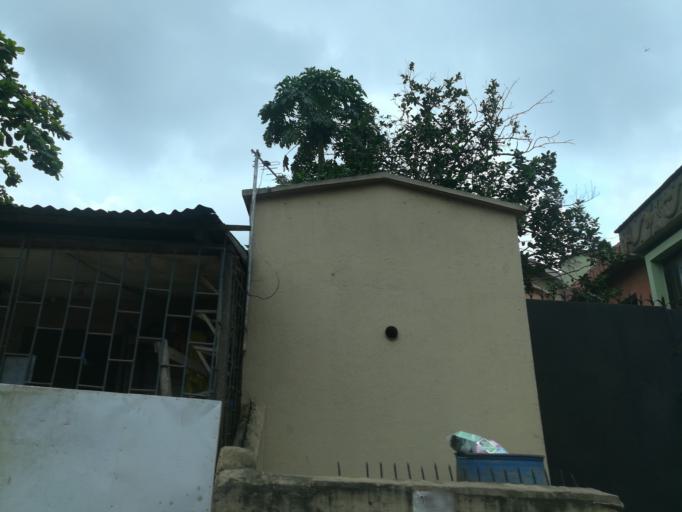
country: NG
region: Lagos
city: Oshodi
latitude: 6.5566
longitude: 3.3365
